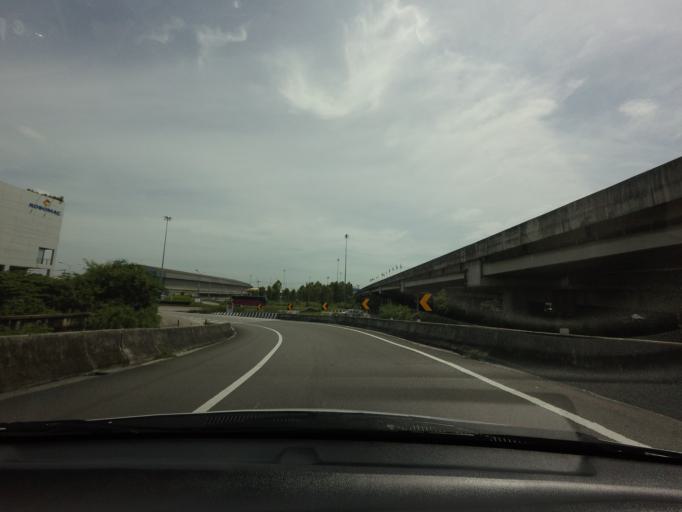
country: TH
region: Bangkok
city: Bang Na
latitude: 13.6148
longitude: 100.6607
